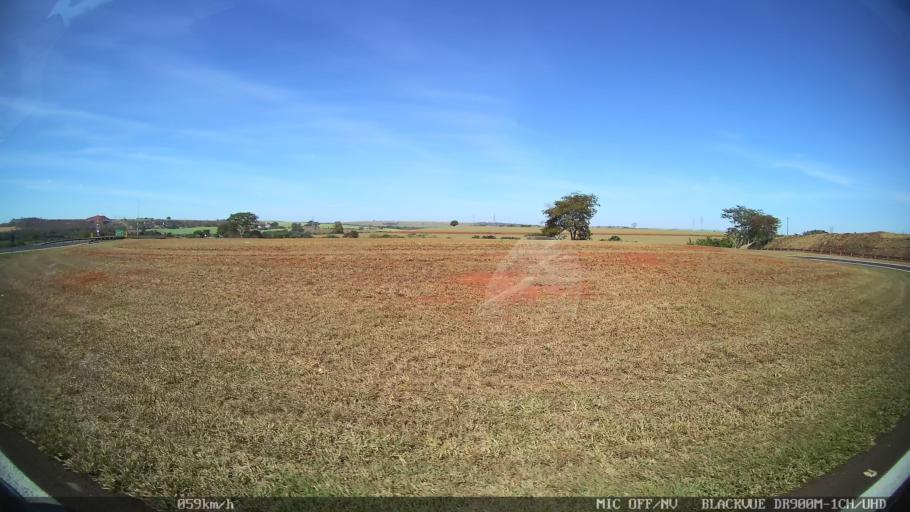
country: BR
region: Sao Paulo
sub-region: Sao Joaquim Da Barra
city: Sao Joaquim da Barra
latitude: -20.5244
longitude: -47.8423
